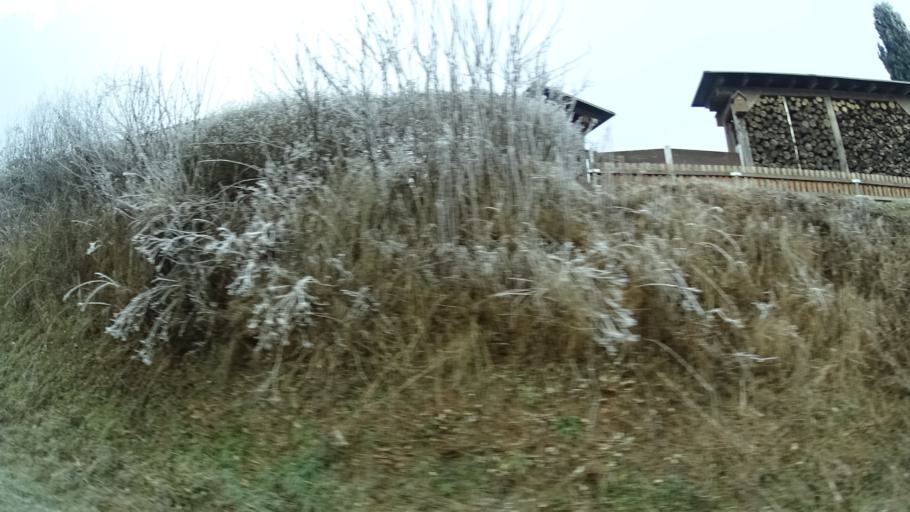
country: DE
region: Bavaria
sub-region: Regierungsbezirk Unterfranken
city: Wiesen
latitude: 50.1105
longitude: 9.3613
